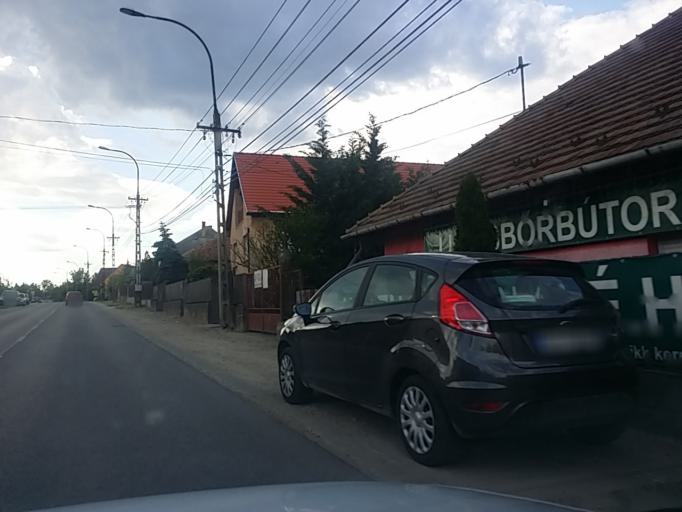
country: HU
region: Pest
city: Veresegyhaz
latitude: 47.6541
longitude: 19.2775
